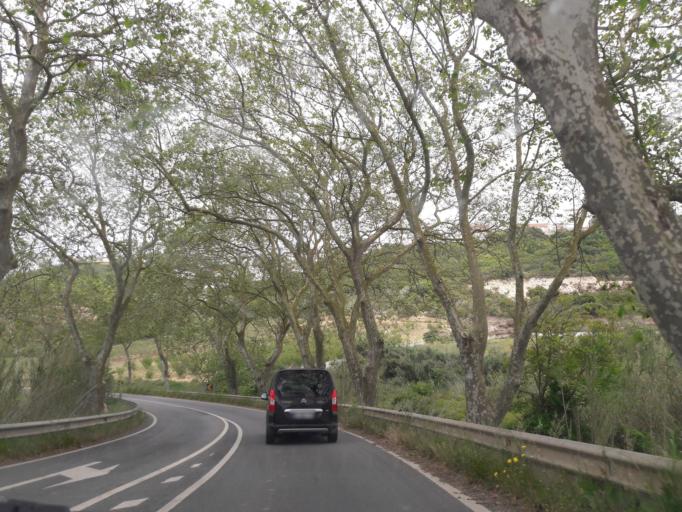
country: PT
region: Leiria
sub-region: Obidos
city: Obidos
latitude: 39.3485
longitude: -9.1816
